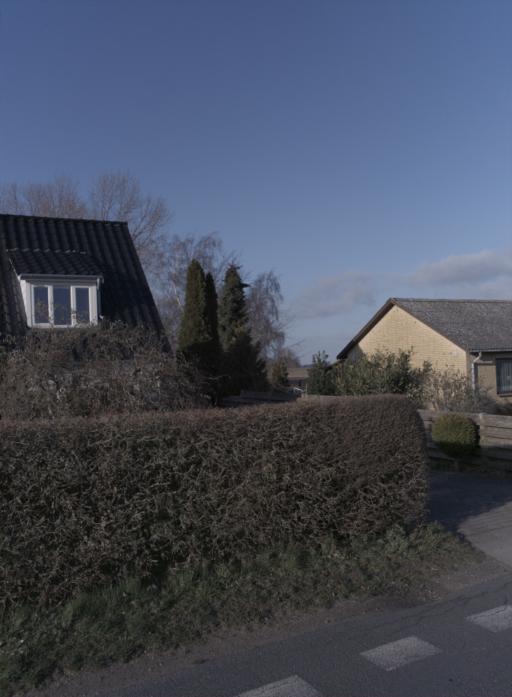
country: DK
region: Zealand
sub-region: Kalundborg Kommune
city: Kalundborg
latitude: 55.6906
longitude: 11.1396
